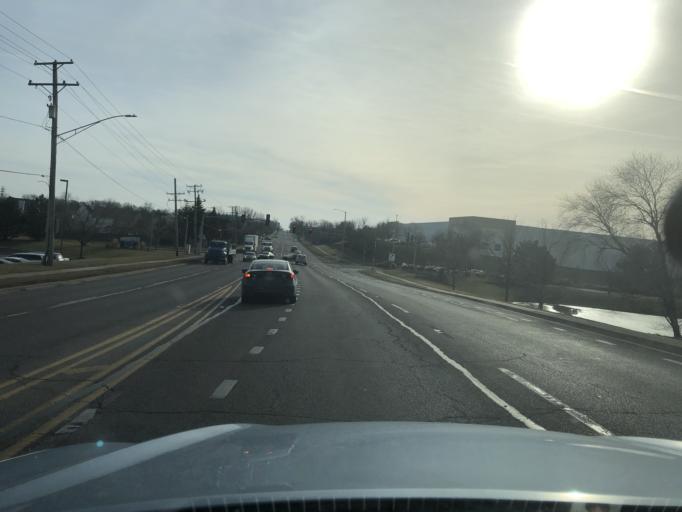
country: US
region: Illinois
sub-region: DuPage County
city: Glendale Heights
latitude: 41.9277
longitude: -88.0809
